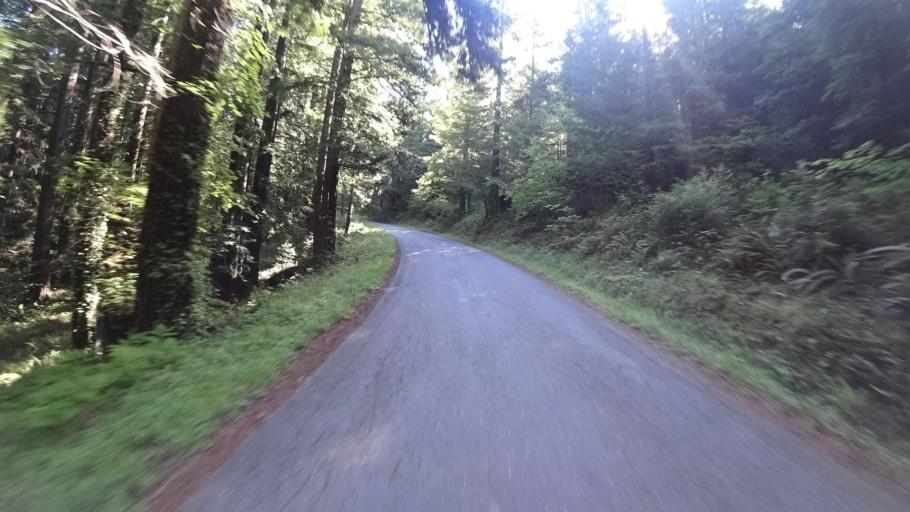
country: US
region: California
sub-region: Humboldt County
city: Rio Dell
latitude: 40.4541
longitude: -124.0278
